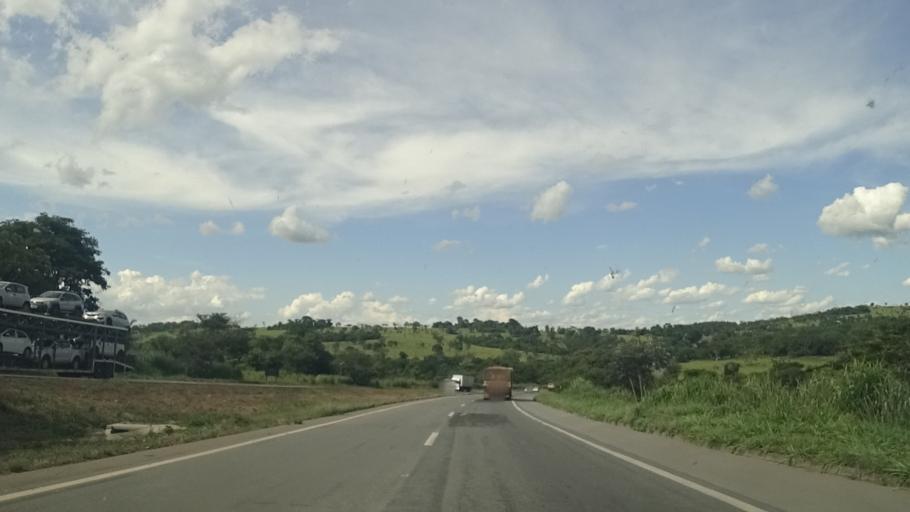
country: BR
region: Goias
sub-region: Piracanjuba
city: Piracanjuba
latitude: -17.2398
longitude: -49.2395
